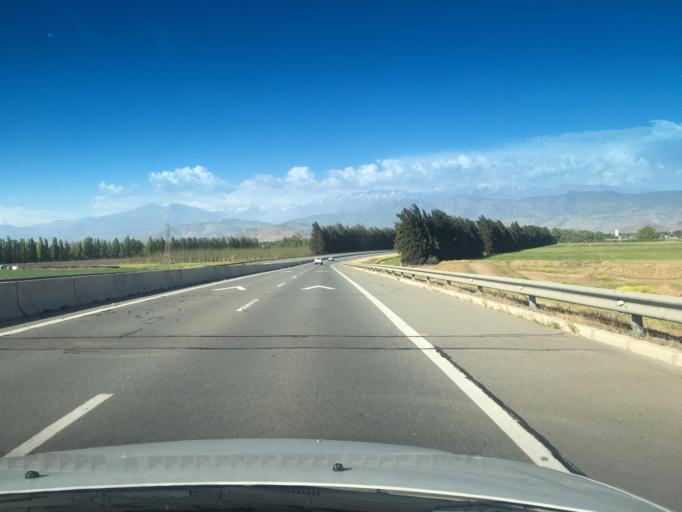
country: CL
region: Santiago Metropolitan
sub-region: Provincia de Chacabuco
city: Chicureo Abajo
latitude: -33.2959
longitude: -70.7218
